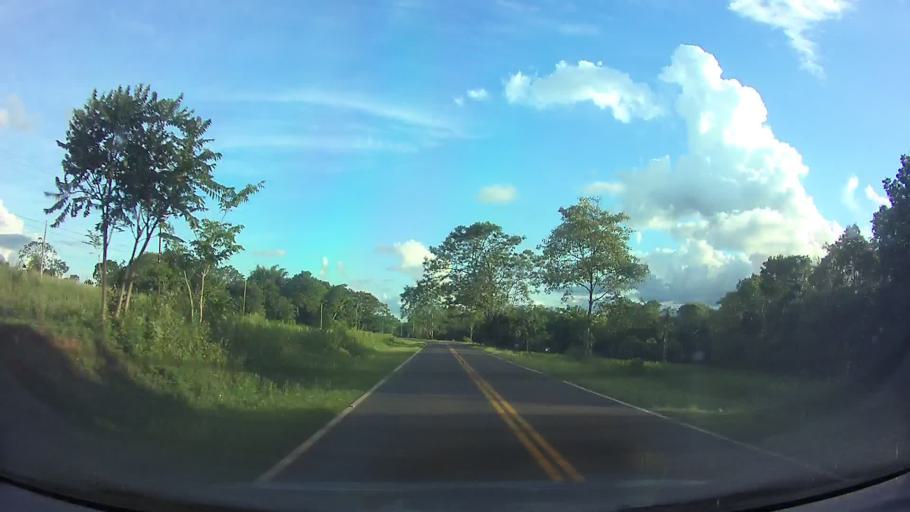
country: PY
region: Paraguari
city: Ybycui
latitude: -25.9595
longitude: -57.0894
